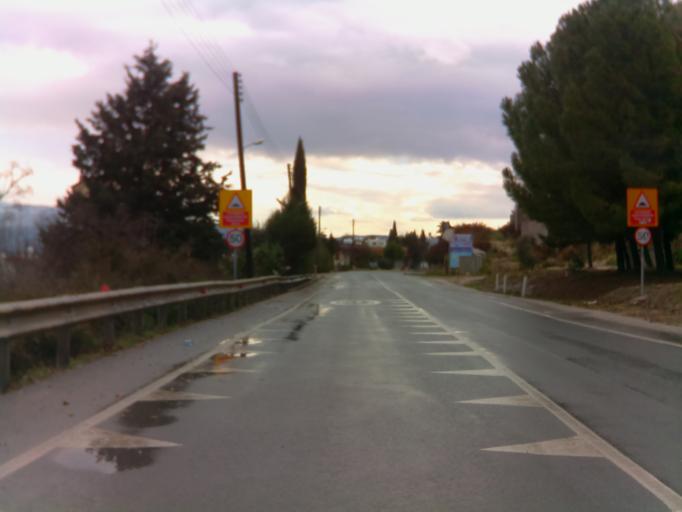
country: CY
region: Pafos
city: Tala
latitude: 34.8916
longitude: 32.4749
